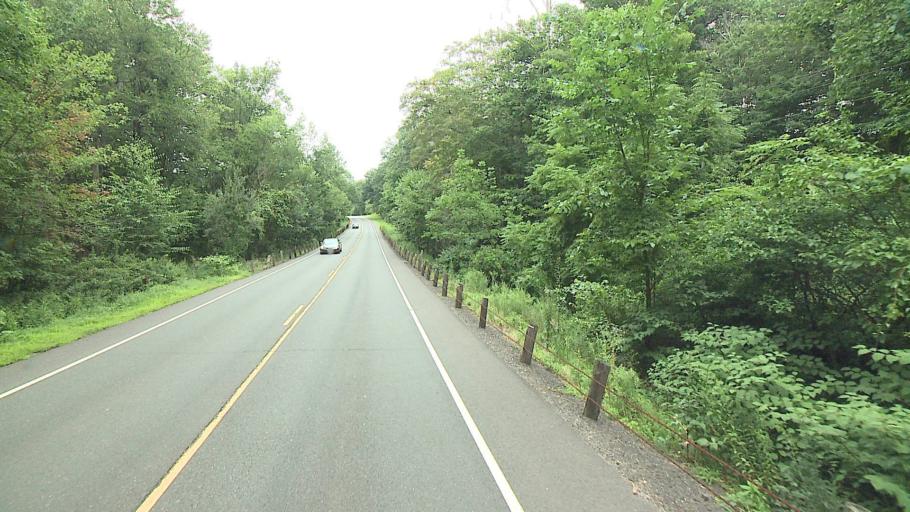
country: US
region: Connecticut
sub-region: New Haven County
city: Middlebury
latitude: 41.5313
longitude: -73.1258
